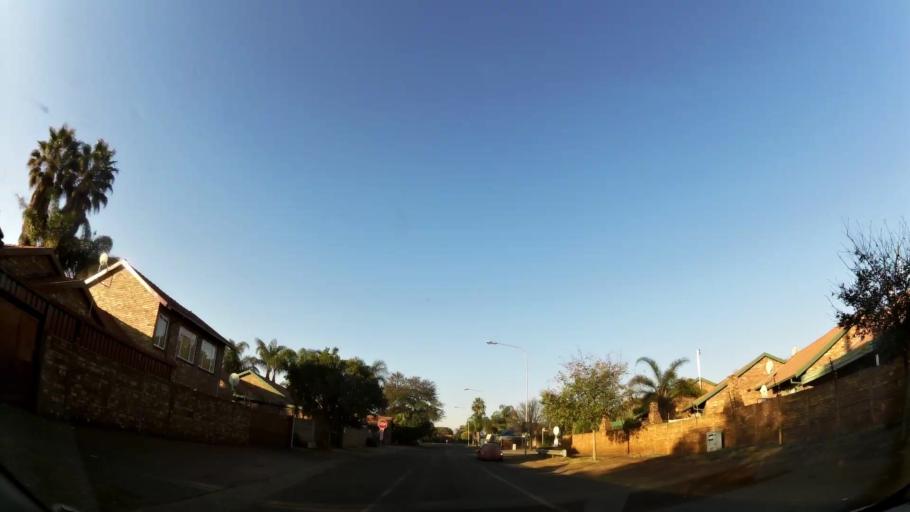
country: ZA
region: Gauteng
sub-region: City of Tshwane Metropolitan Municipality
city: Centurion
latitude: -25.8724
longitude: 28.1416
